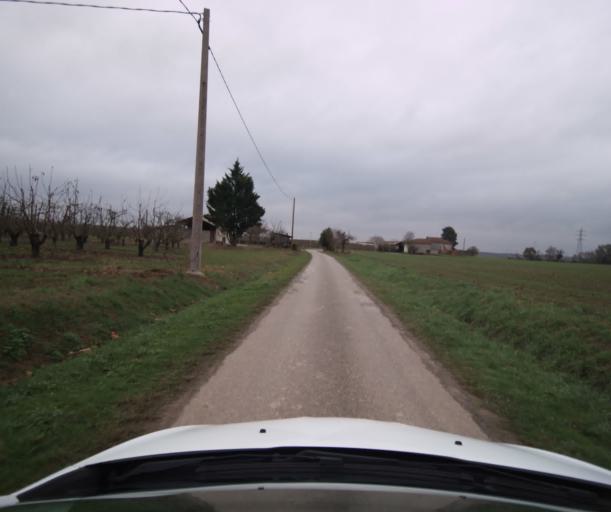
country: FR
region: Midi-Pyrenees
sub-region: Departement du Tarn-et-Garonne
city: Moissac
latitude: 44.1010
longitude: 1.1562
